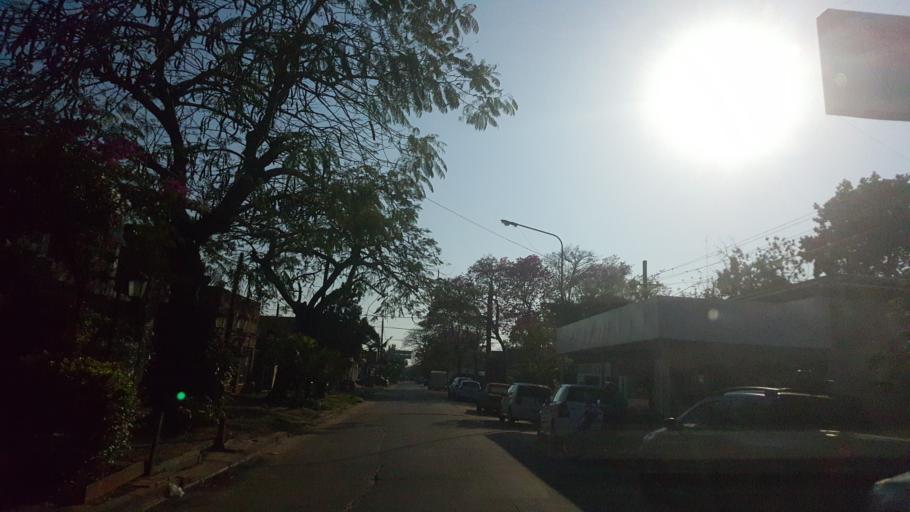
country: AR
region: Corrientes
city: Ituzaingo
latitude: -27.5836
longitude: -56.6847
